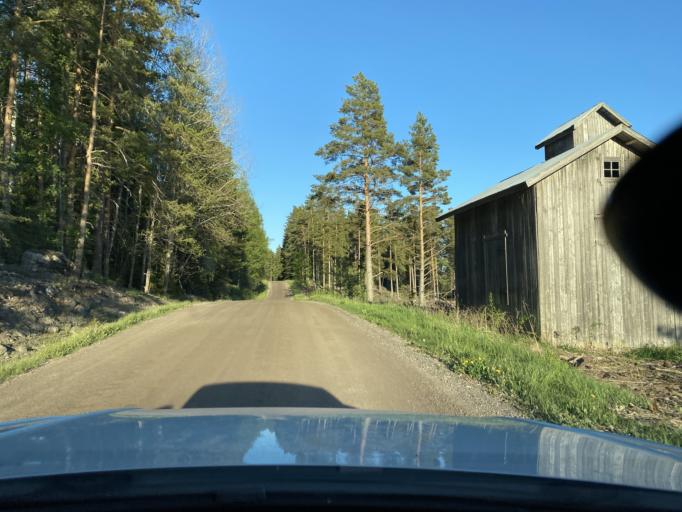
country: FI
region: Satakunta
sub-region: Rauma
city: Lappi
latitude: 61.1374
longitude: 21.9649
